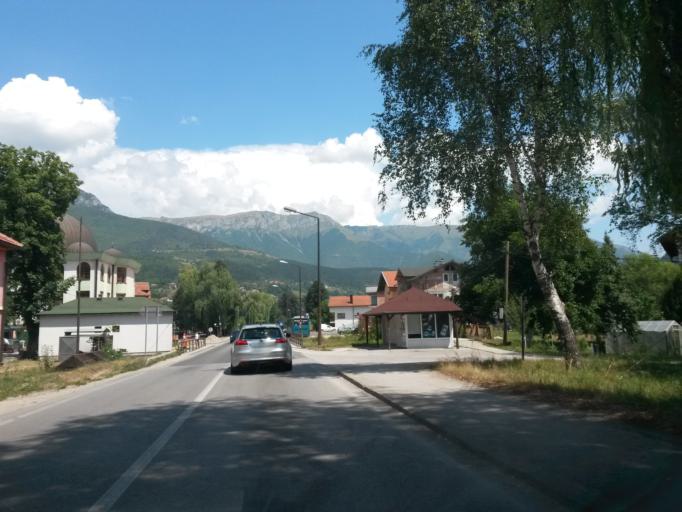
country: BA
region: Federation of Bosnia and Herzegovina
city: Turbe
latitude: 44.2398
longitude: 17.5750
